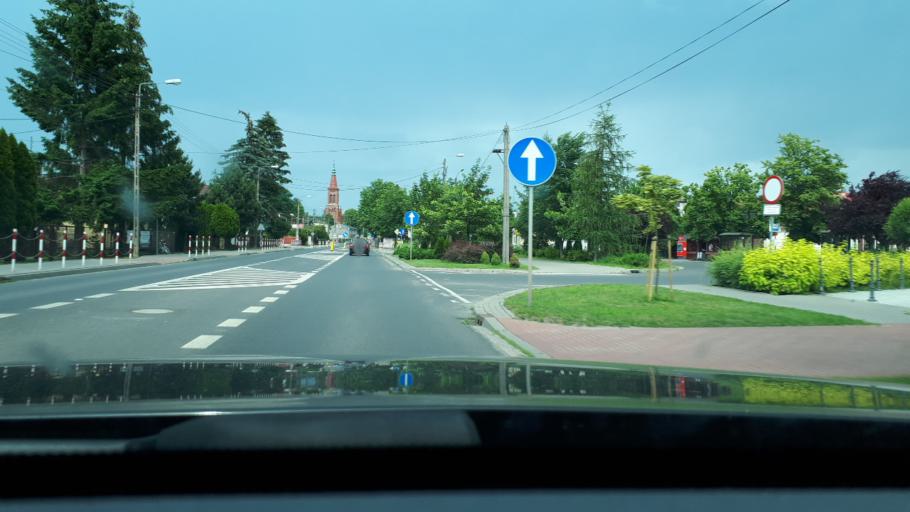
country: PL
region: Masovian Voivodeship
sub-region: Powiat warszawski zachodni
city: Leszno
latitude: 52.2577
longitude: 20.5854
